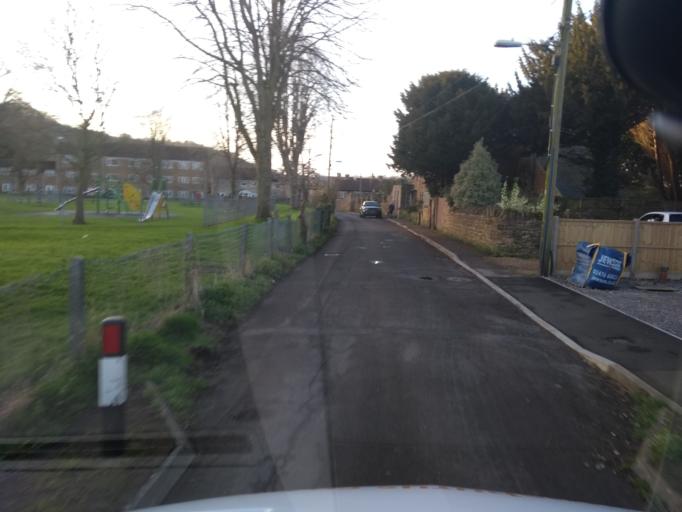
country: GB
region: England
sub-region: Somerset
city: Stoke-sub-Hamdon
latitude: 50.9534
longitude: -2.7530
